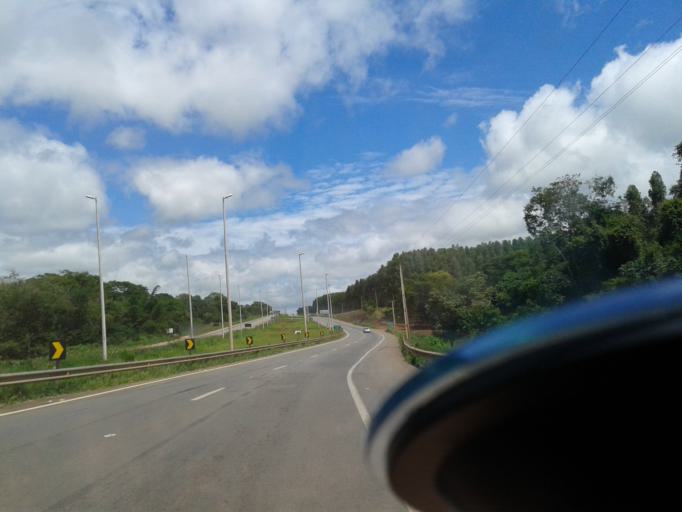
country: BR
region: Goias
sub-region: Goianira
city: Goianira
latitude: -16.4405
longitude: -49.4563
